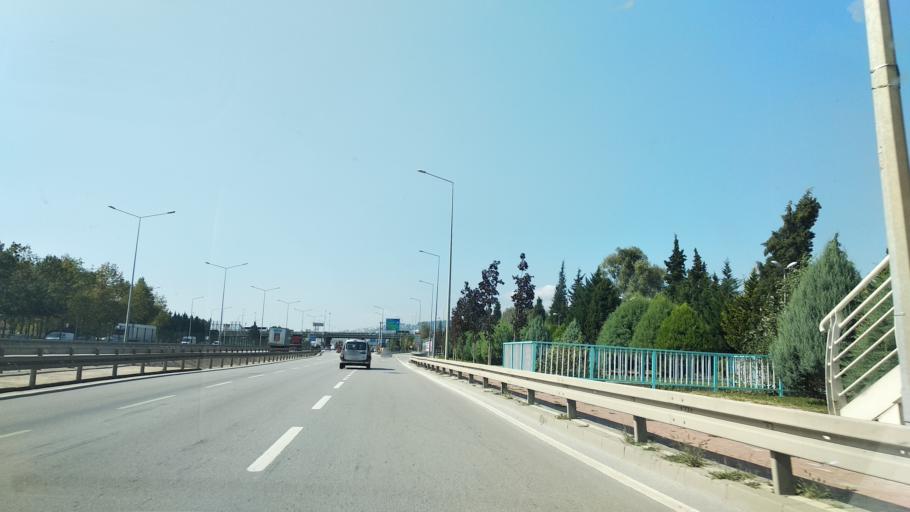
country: TR
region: Kocaeli
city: Kullar
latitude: 40.7613
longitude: 29.9705
